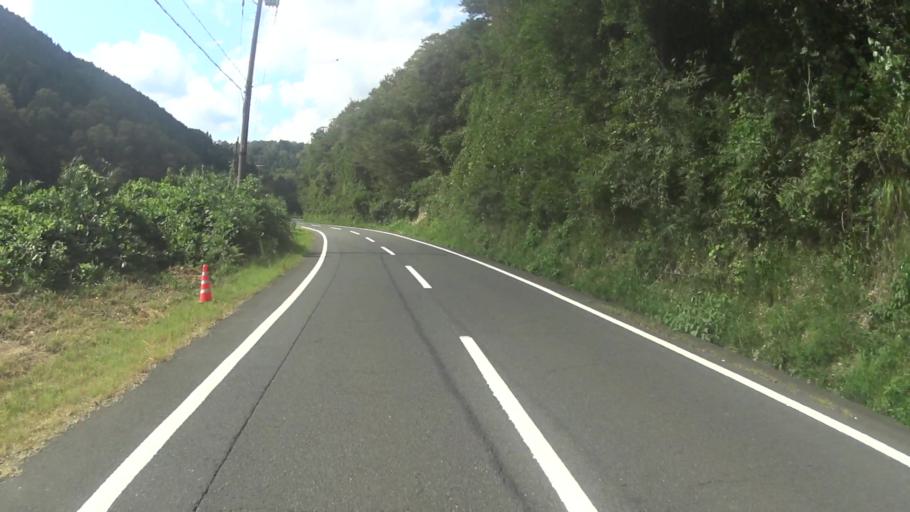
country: JP
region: Kyoto
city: Miyazu
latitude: 35.7098
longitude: 135.2631
